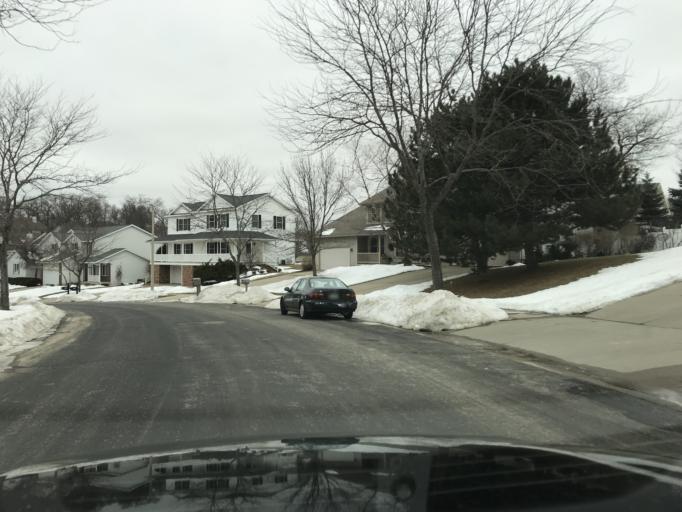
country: US
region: Wisconsin
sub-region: Dane County
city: Monona
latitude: 43.0770
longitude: -89.2751
